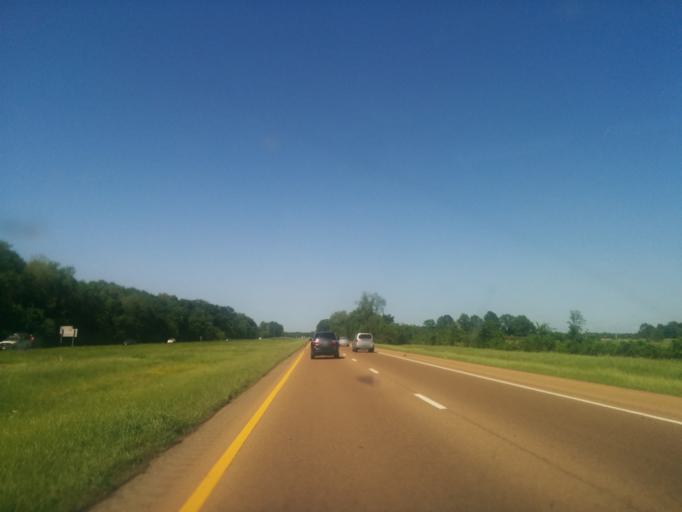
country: US
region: Mississippi
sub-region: Madison County
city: Madison
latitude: 32.4886
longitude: -90.1285
